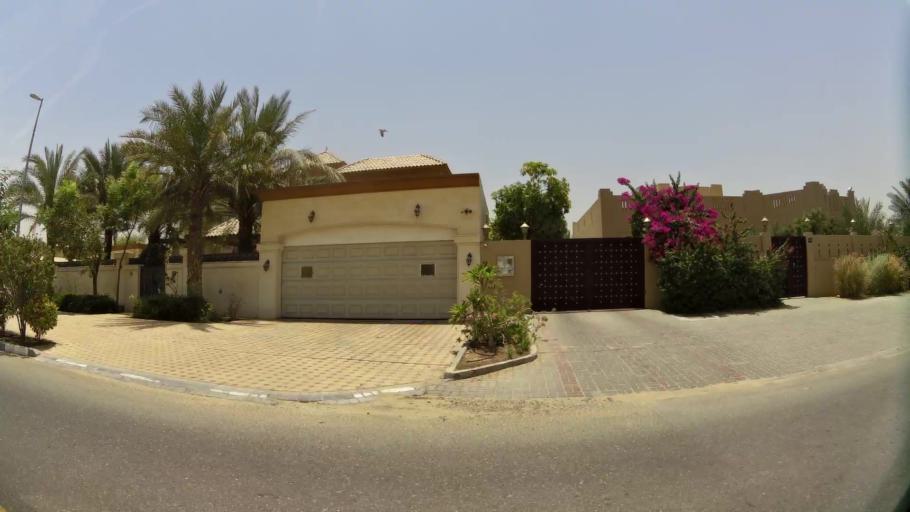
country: AE
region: Ash Shariqah
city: Sharjah
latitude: 25.2541
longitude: 55.4569
